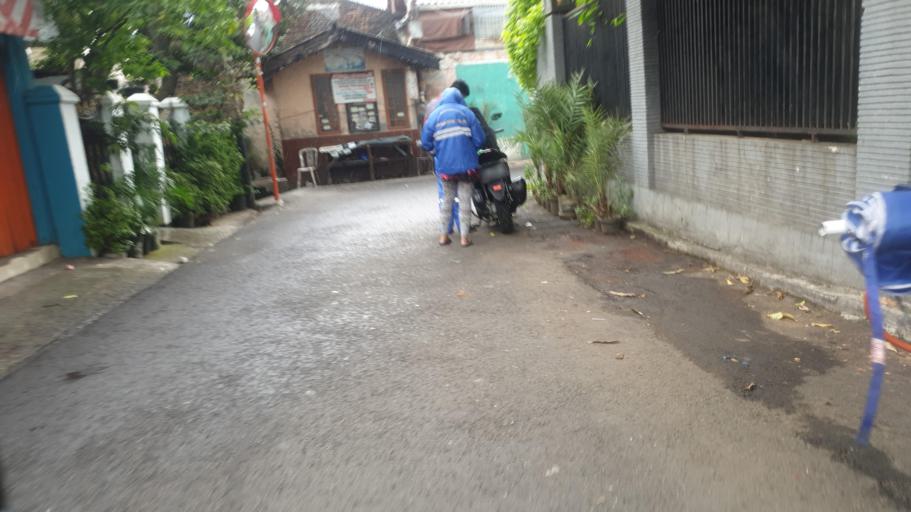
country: ID
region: Jakarta Raya
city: Jakarta
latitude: -6.2584
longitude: 106.7874
